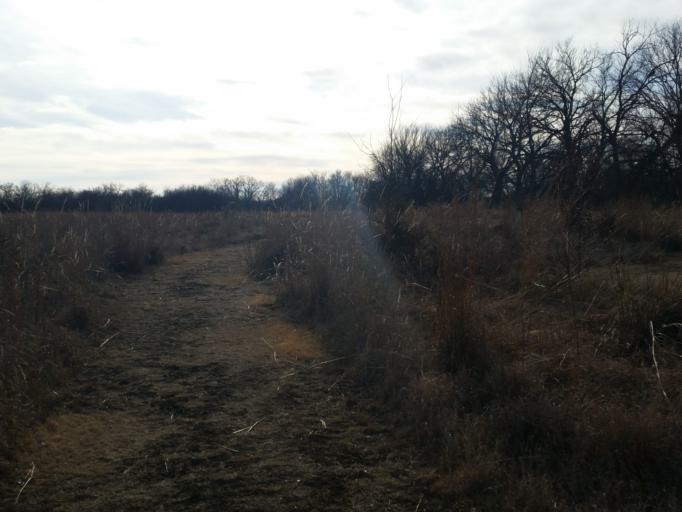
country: US
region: Kansas
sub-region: Harvey County
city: North Newton
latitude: 38.0633
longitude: -97.3389
